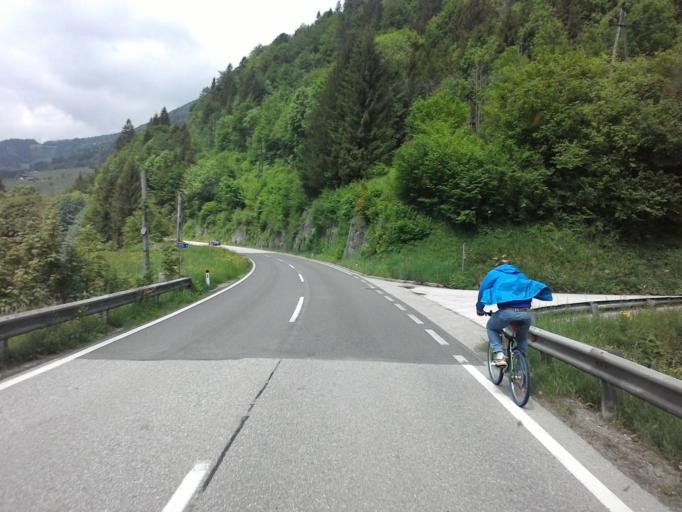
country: AT
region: Upper Austria
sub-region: Politischer Bezirk Steyr-Land
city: Maria Neustift
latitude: 47.8785
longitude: 14.6025
